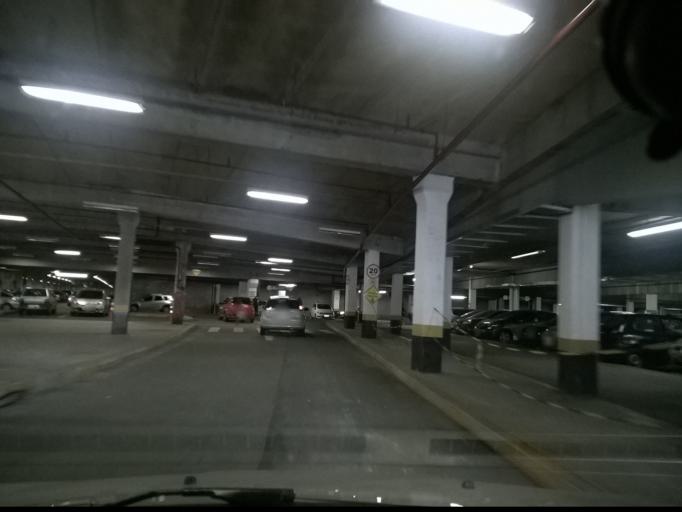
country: BR
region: Sao Paulo
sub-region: Osasco
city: Osasco
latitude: -23.5364
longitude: -46.7717
